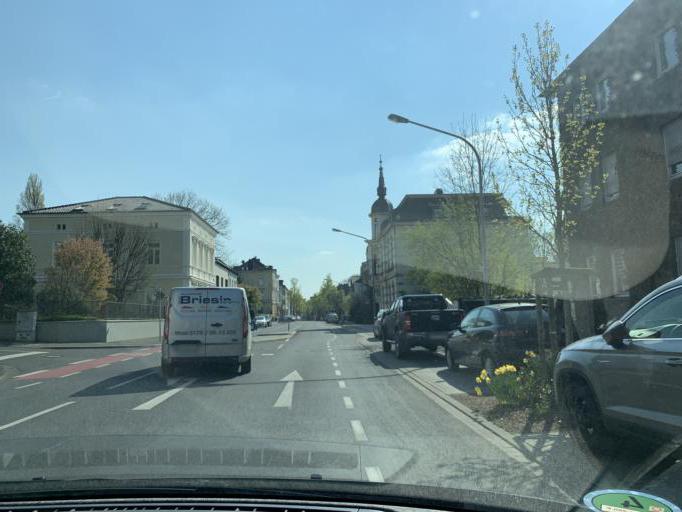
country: DE
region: North Rhine-Westphalia
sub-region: Regierungsbezirk Dusseldorf
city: Monchengladbach
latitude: 51.1379
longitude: 6.4539
